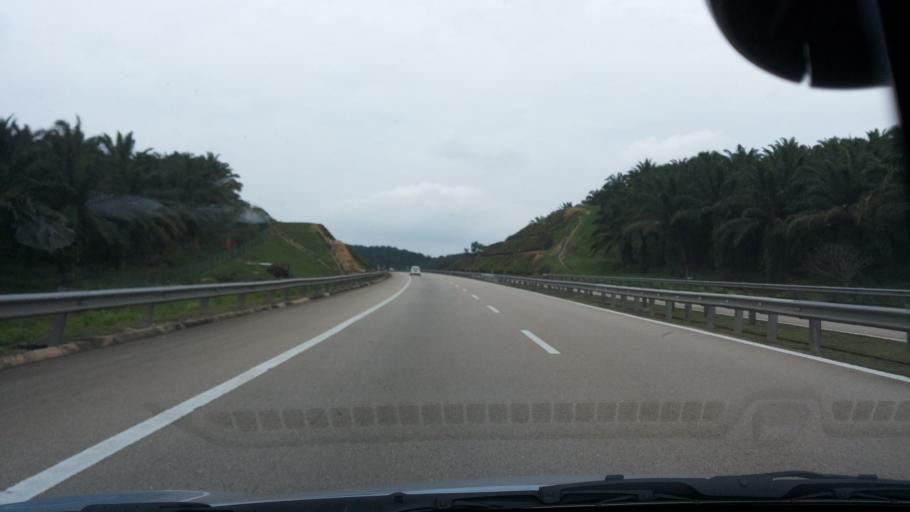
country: MY
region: Pahang
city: Kuantan
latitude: 3.7810
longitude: 103.1538
